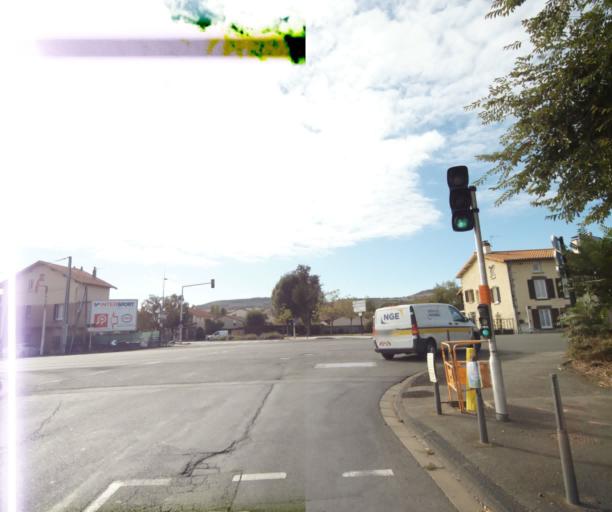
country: FR
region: Auvergne
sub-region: Departement du Puy-de-Dome
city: Aulnat
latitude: 45.7759
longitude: 3.1925
